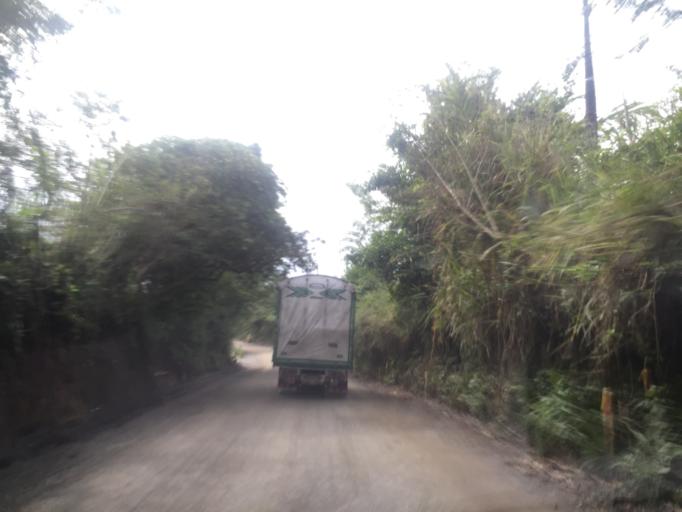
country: CO
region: Quindio
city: La Tebaida
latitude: 4.4585
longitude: -75.7939
